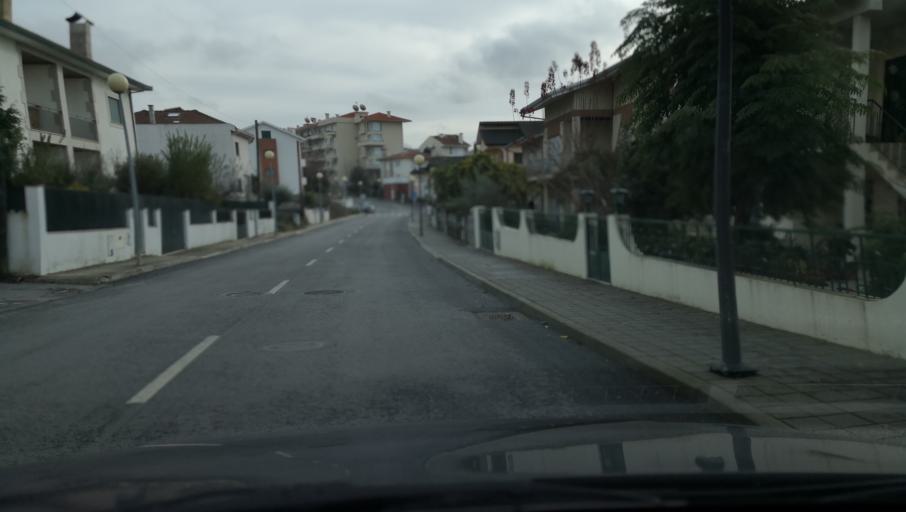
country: PT
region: Vila Real
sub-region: Vila Real
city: Vila Real
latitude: 41.2939
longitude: -7.7281
